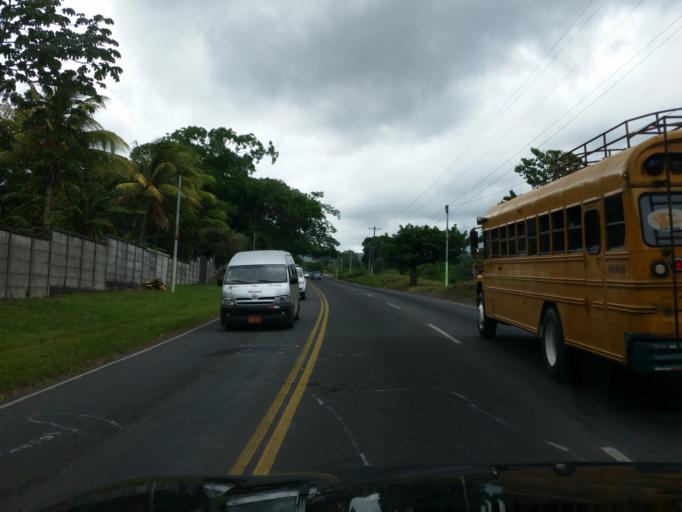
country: NI
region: Managua
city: El Crucero
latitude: 12.0496
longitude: -86.3144
